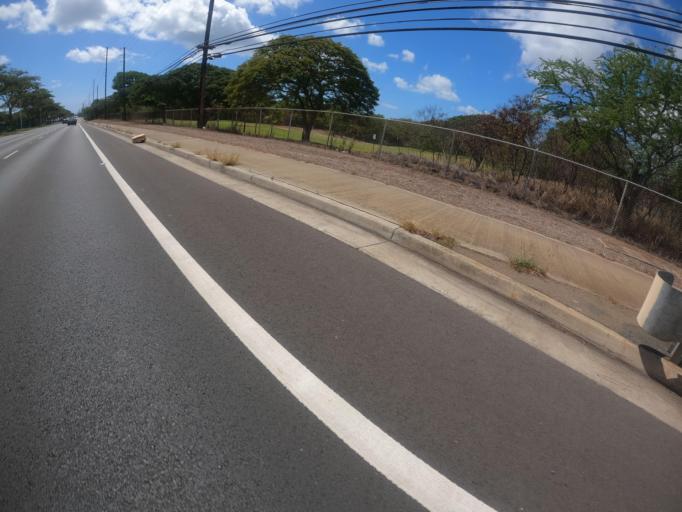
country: US
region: Hawaii
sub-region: Honolulu County
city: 'Ewa Gentry
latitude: 21.3530
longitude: -158.0285
